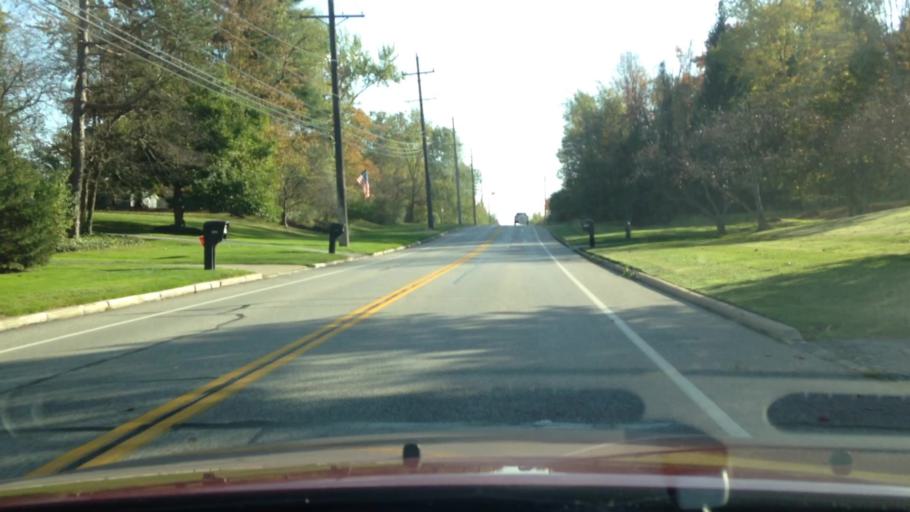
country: US
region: Ohio
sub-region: Cuyahoga County
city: Pepper Pike
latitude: 41.4747
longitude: -81.4634
